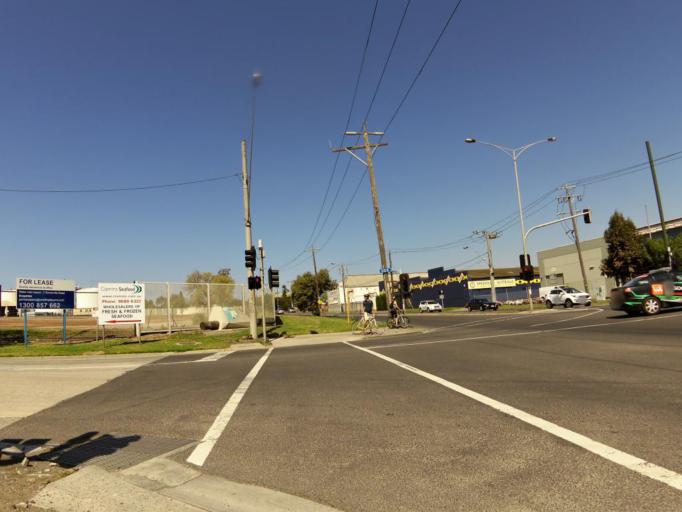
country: AU
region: Victoria
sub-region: Maribyrnong
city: Yarraville
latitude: -37.8145
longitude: 144.9001
